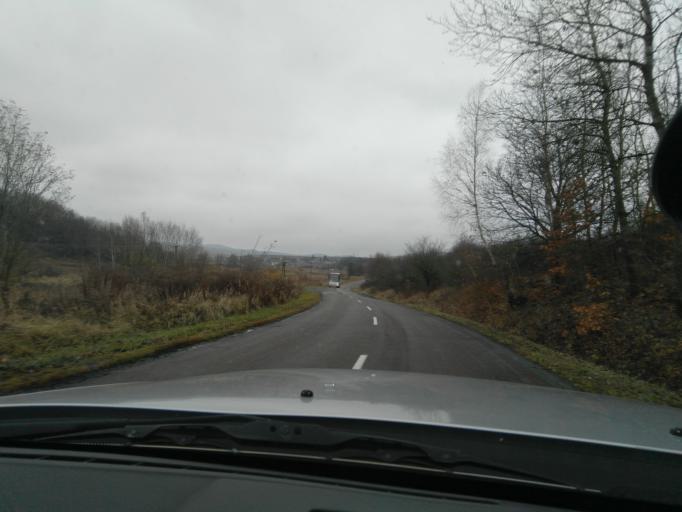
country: HU
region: Nograd
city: Matraterenye
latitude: 48.0439
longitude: 19.9174
